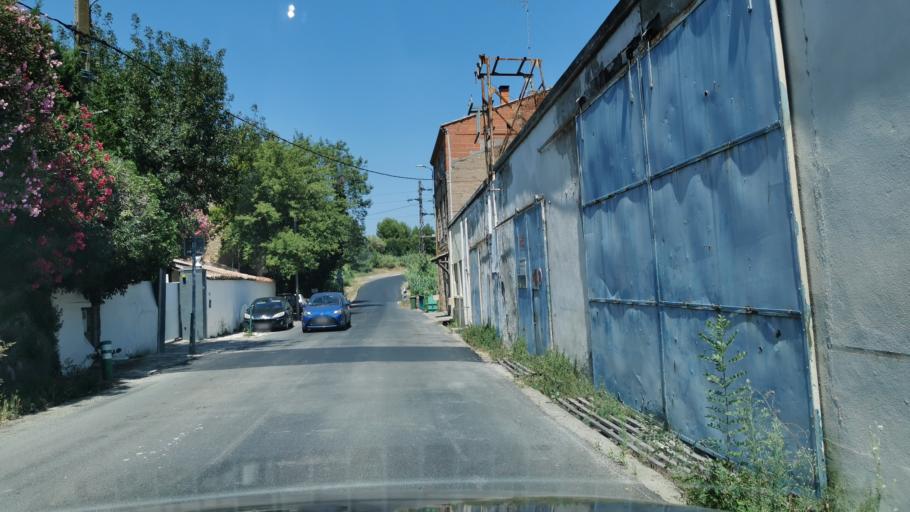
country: FR
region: Languedoc-Roussillon
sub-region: Departement de l'Herault
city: Cazouls-les-Beziers
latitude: 43.3963
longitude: 3.1033
